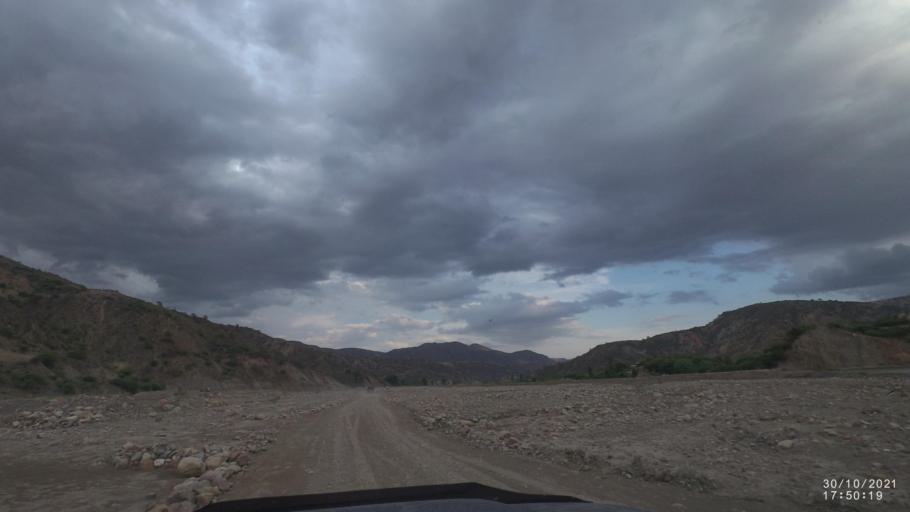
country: BO
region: Cochabamba
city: Sipe Sipe
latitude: -17.5365
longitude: -66.5106
